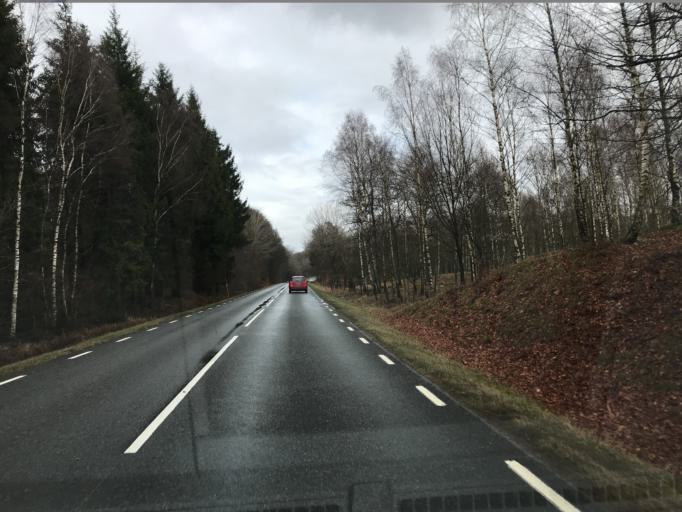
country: SE
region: Skane
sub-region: Hassleholms Kommun
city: Tormestorp
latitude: 56.0837
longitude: 13.7889
